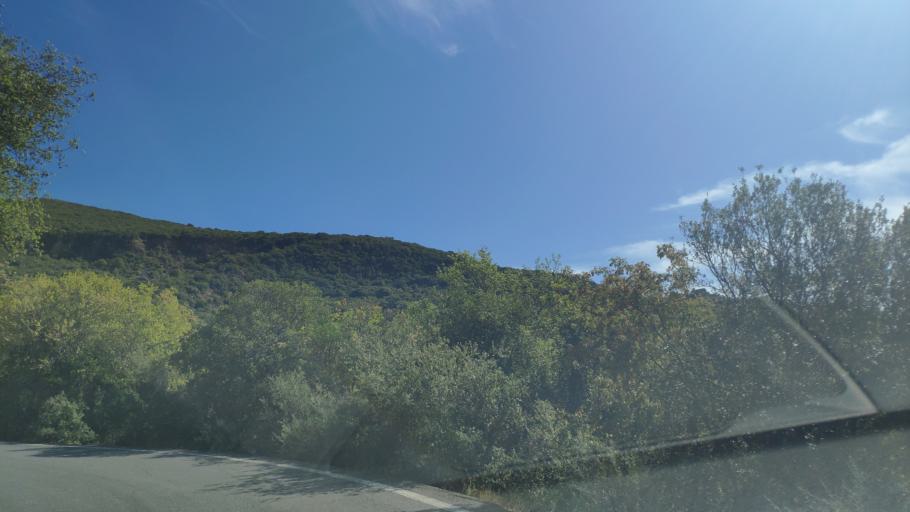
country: GR
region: Peloponnese
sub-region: Nomos Arkadias
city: Dimitsana
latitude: 37.5343
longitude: 22.0498
